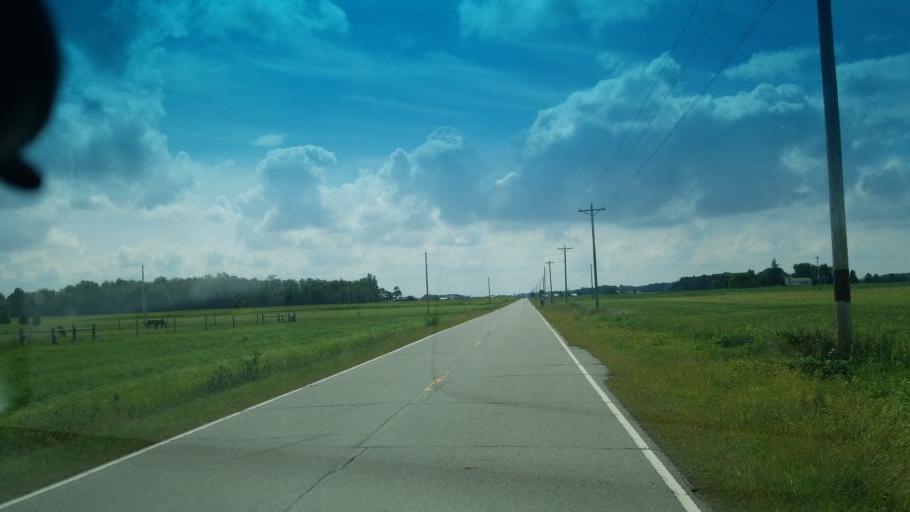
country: US
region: Ohio
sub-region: Crawford County
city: Bucyrus
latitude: 40.9391
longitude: -82.9017
